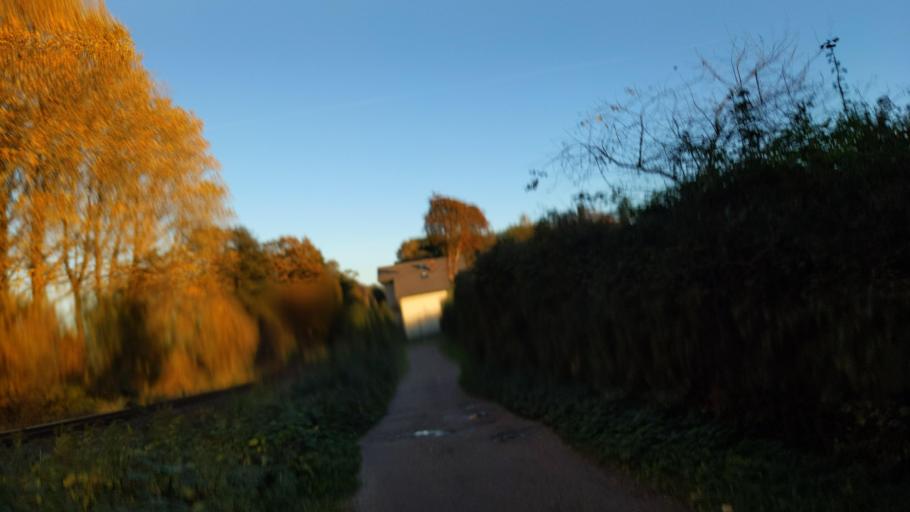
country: DE
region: Schleswig-Holstein
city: Luebeck
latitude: 53.8416
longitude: 10.7219
